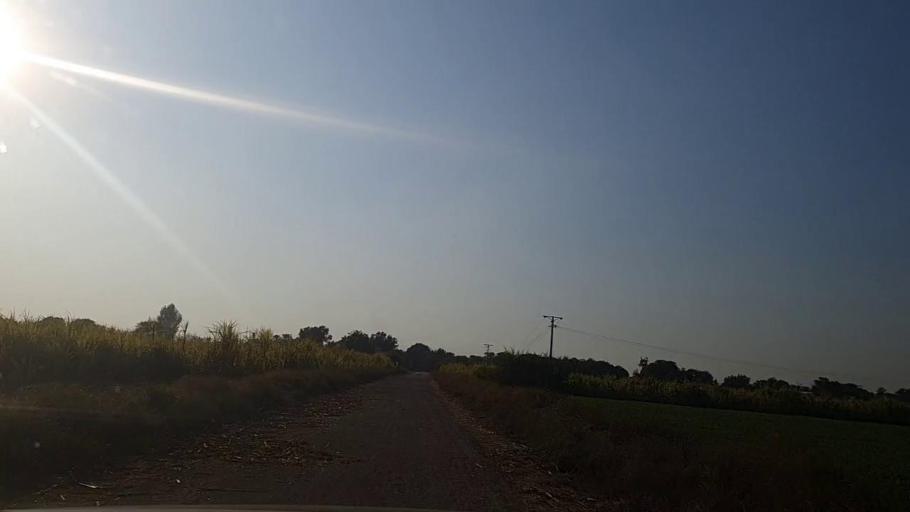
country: PK
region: Sindh
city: Sakrand
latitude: 26.3110
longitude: 68.1452
